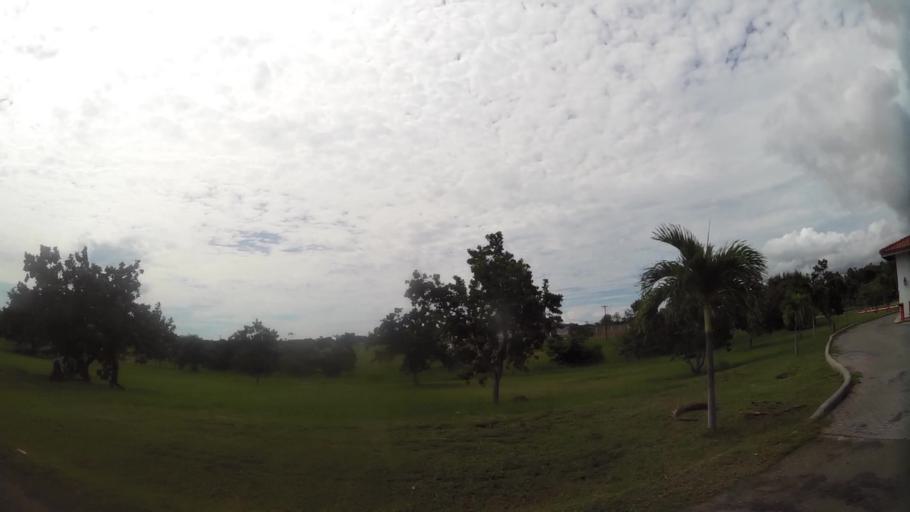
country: PA
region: Panama
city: Nueva Gorgona
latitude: 8.5419
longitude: -79.8985
